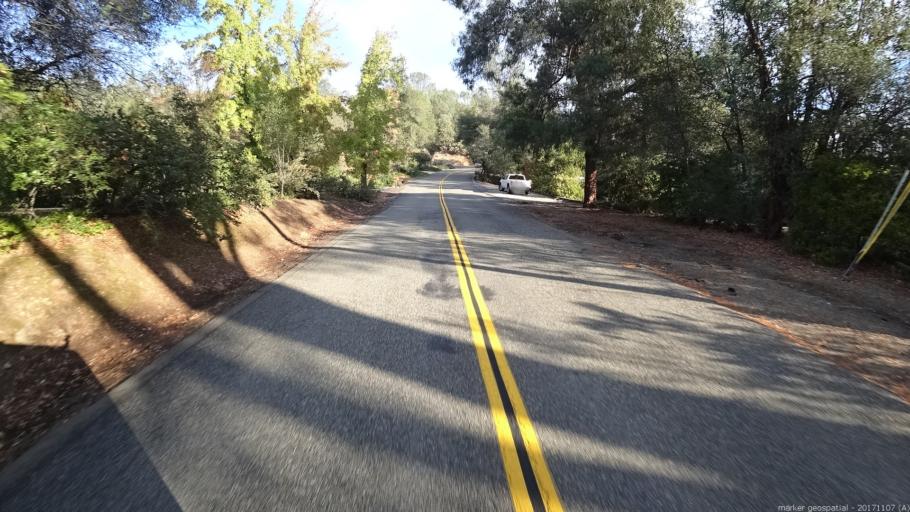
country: US
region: California
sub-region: Shasta County
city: Shasta
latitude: 40.5839
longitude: -122.4672
